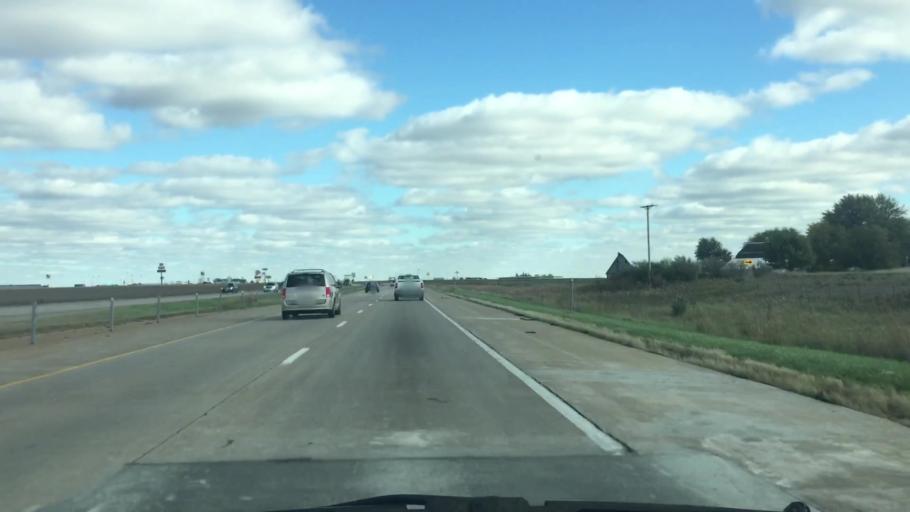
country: US
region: Iowa
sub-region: Scott County
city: Walcott
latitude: 41.6214
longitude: -90.8036
